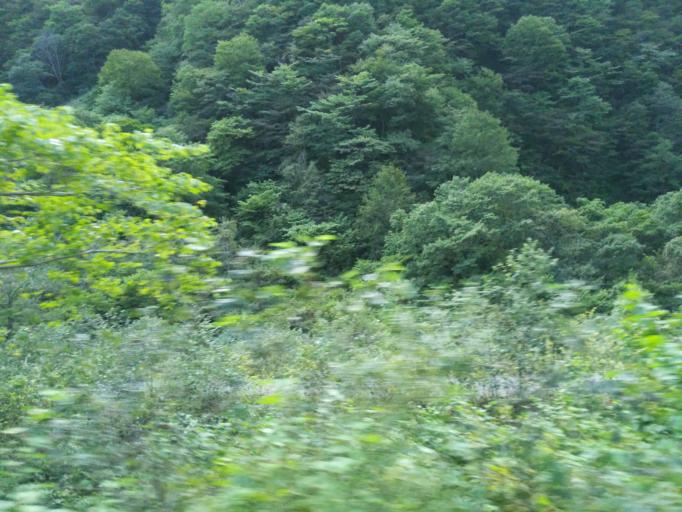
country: JP
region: Toyama
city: Kamiichi
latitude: 36.5318
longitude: 137.4480
